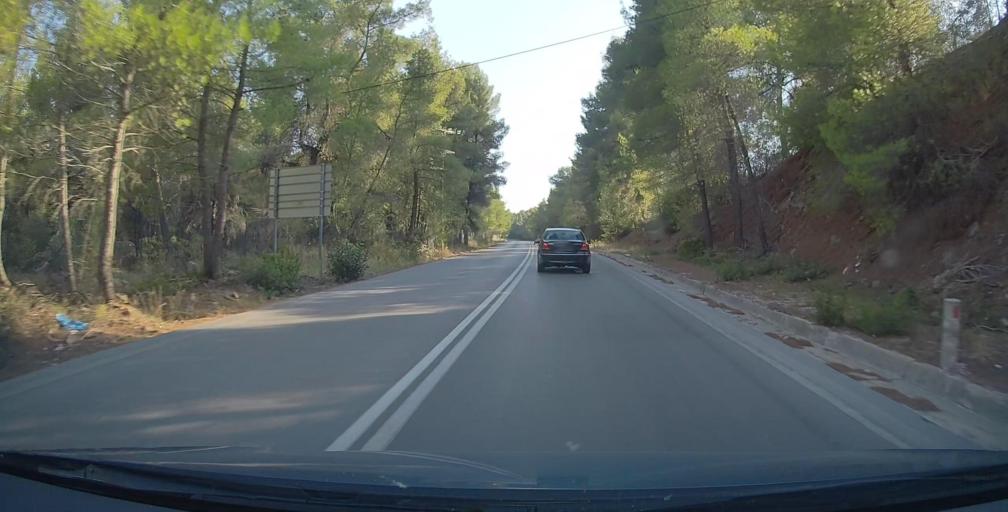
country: GR
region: Central Macedonia
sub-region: Nomos Chalkidikis
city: Neos Marmaras
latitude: 40.0706
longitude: 23.8051
